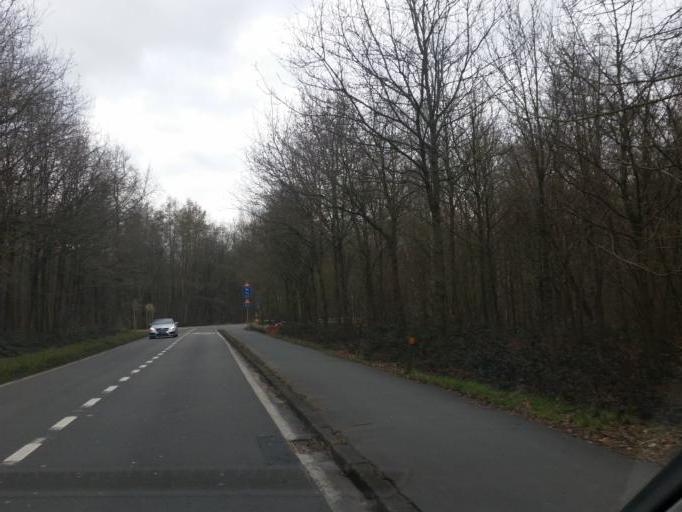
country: BE
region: Flanders
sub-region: Provincie Vlaams-Brabant
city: Sint-Genesius-Rode
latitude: 50.7753
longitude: 4.3915
